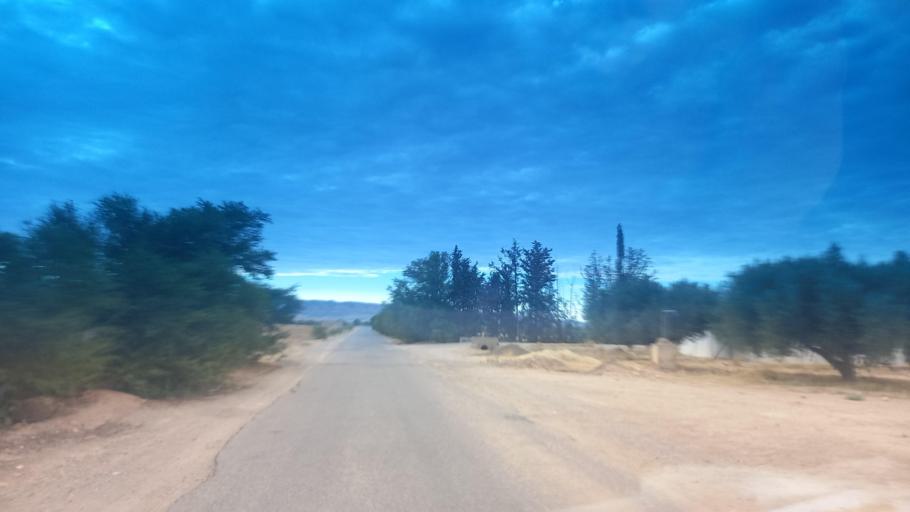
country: TN
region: Al Qasrayn
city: Sbiba
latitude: 35.3755
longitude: 9.0664
